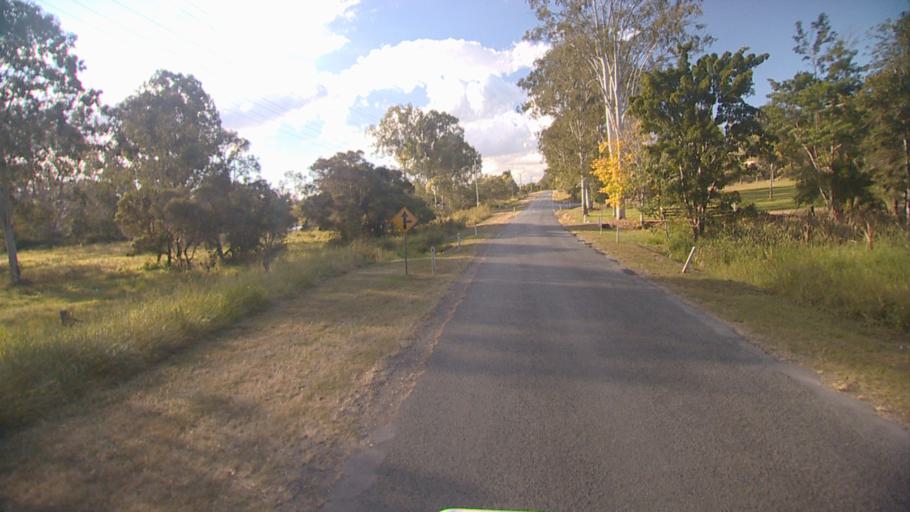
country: AU
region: Queensland
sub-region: Ipswich
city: Springfield Lakes
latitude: -27.7386
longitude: 152.9433
